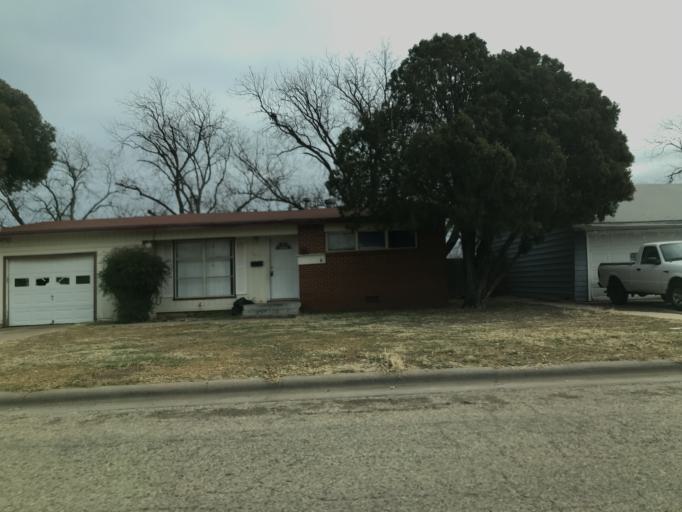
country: US
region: Texas
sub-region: Taylor County
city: Abilene
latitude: 32.4686
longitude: -99.7589
